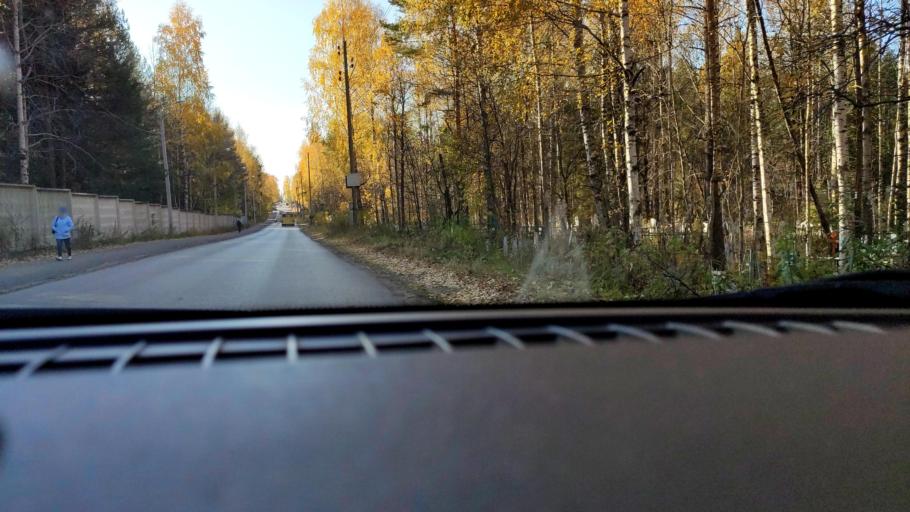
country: RU
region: Perm
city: Kondratovo
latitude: 58.0634
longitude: 56.1254
